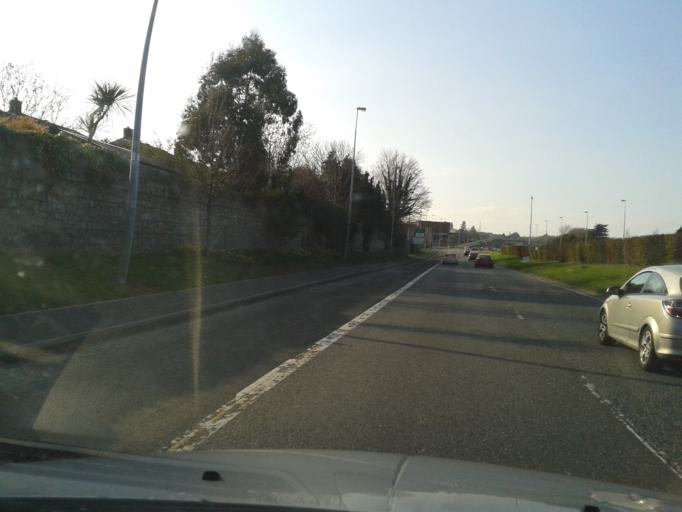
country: IE
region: Leinster
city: Cabinteely
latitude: 53.2642
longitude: -6.1548
